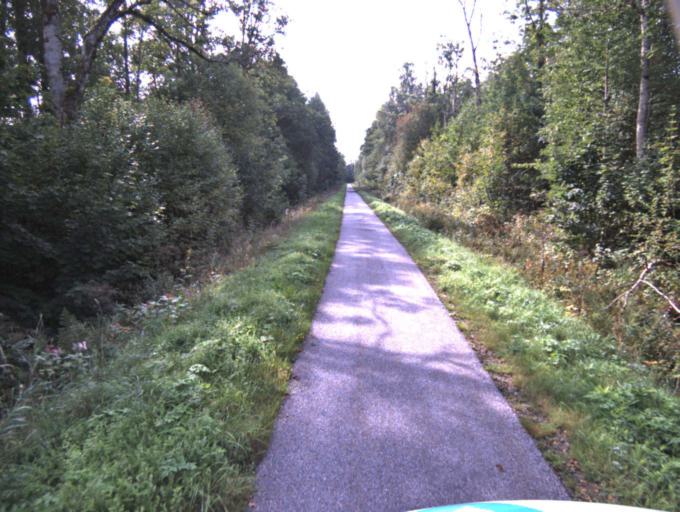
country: SE
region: Vaestra Goetaland
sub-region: Tranemo Kommun
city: Limmared
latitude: 57.6610
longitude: 13.3627
